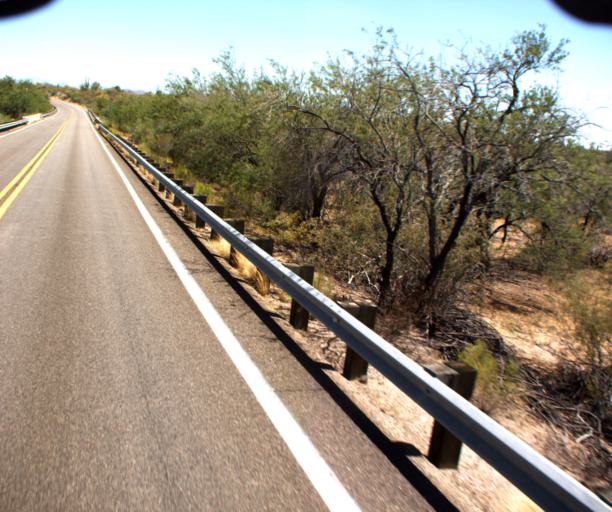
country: US
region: Arizona
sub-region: Pima County
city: Catalina
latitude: 32.6774
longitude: -111.0696
